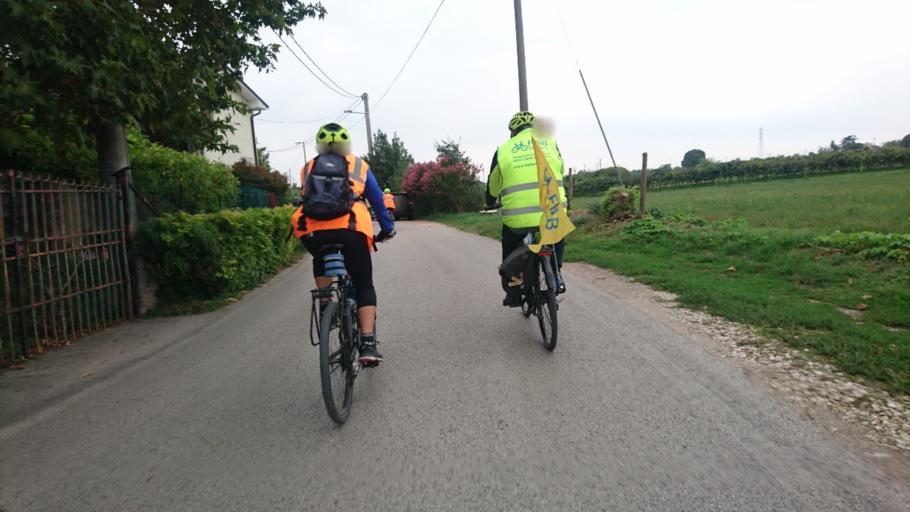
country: IT
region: Veneto
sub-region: Provincia di Verona
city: San Giovanni Lupatoto
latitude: 45.4157
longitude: 11.0572
